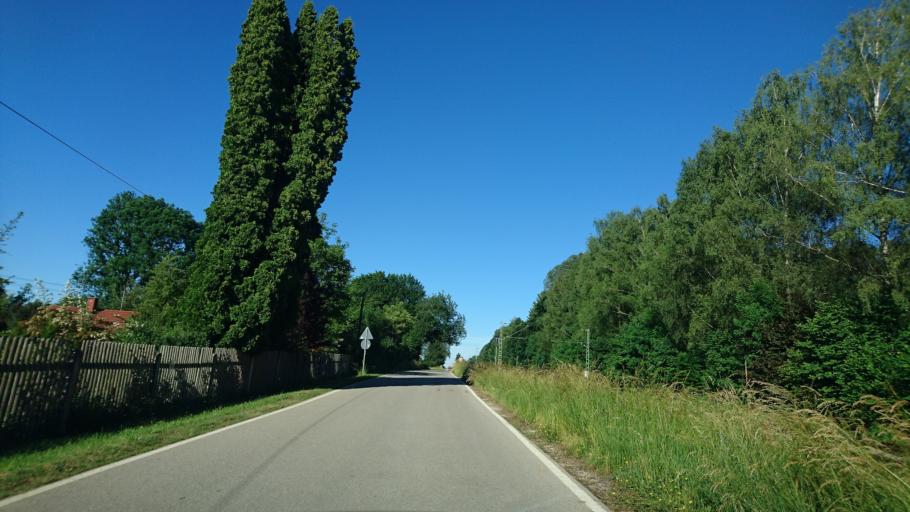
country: DE
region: Bavaria
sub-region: Upper Bavaria
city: Poing
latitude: 48.1743
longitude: 11.8212
